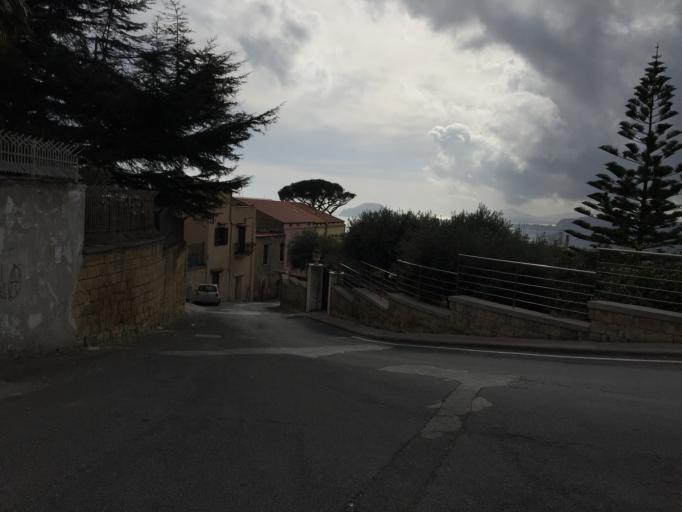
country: IT
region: Campania
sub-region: Provincia di Napoli
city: Pozzuoli
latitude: 40.8272
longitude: 14.1348
